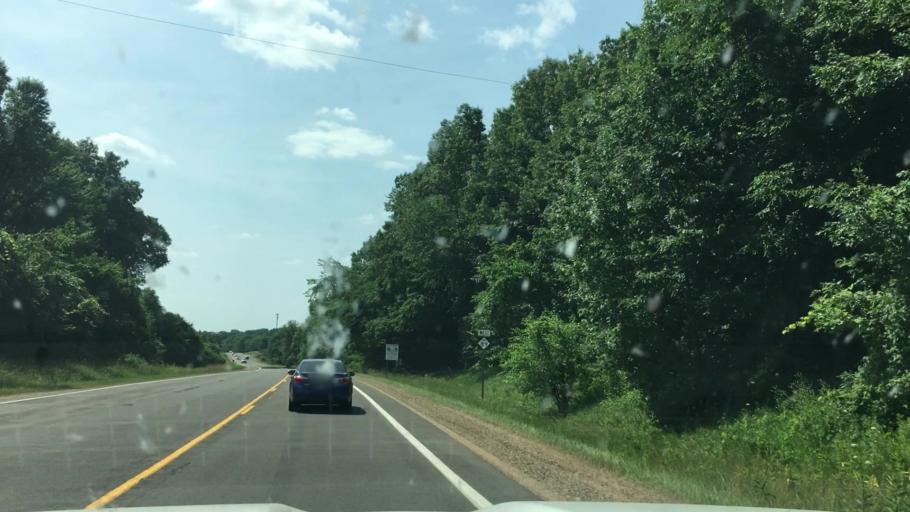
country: US
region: Michigan
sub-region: Allegan County
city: Plainwell
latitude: 42.4323
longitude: -85.5529
